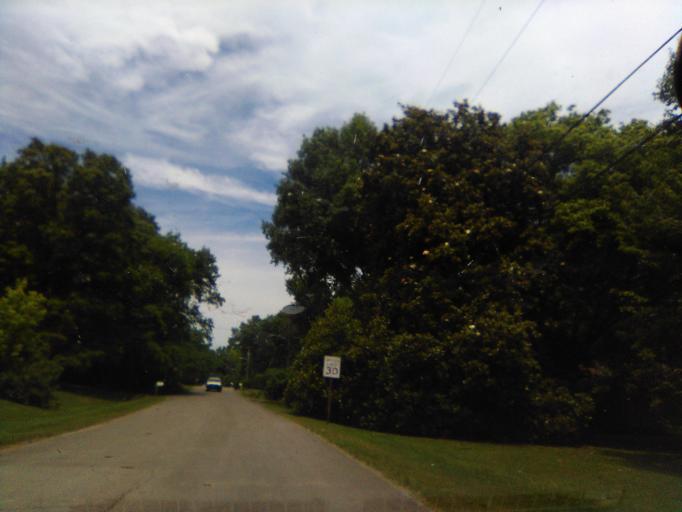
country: US
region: Tennessee
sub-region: Davidson County
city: Belle Meade
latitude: 36.1204
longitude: -86.9039
